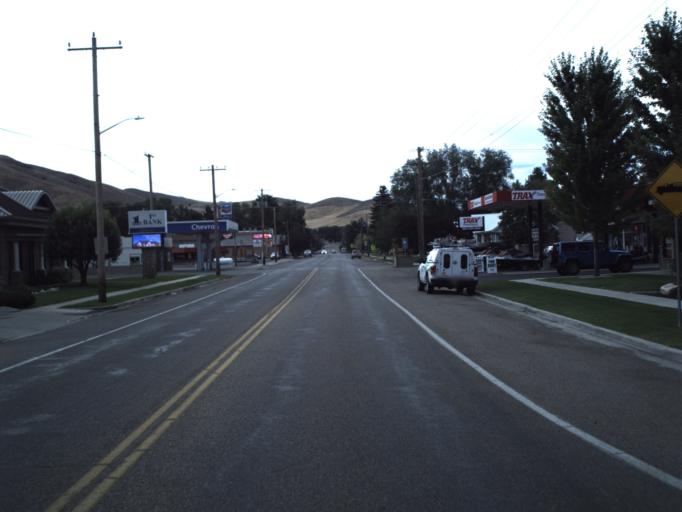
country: US
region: Utah
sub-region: Morgan County
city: Morgan
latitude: 41.0386
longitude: -111.6787
